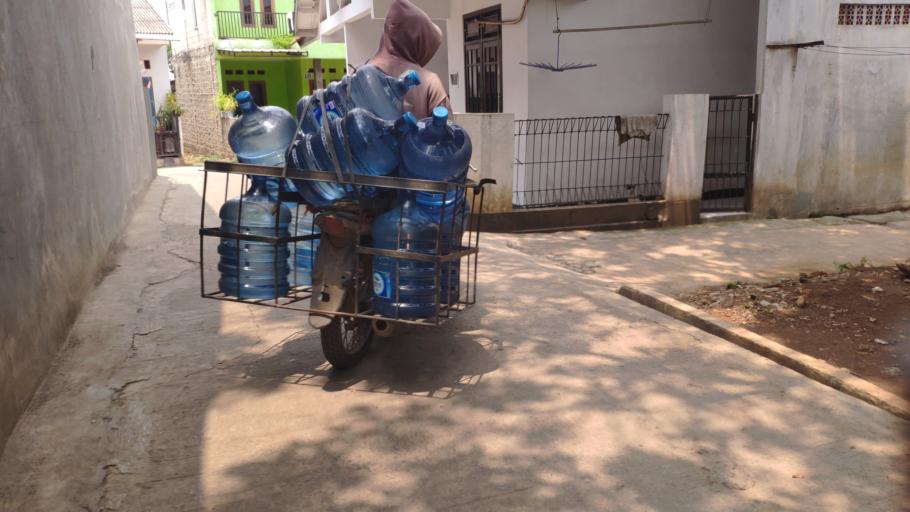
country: ID
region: West Java
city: Sawangan
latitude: -6.3877
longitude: 106.7914
